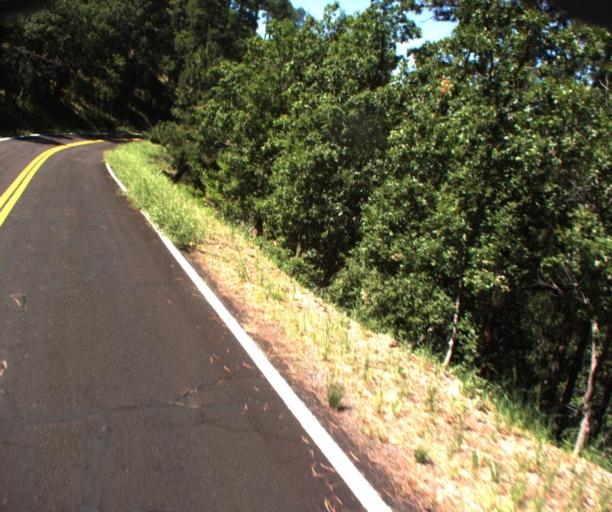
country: US
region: Arizona
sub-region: Greenlee County
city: Morenci
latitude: 33.4433
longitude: -109.3738
